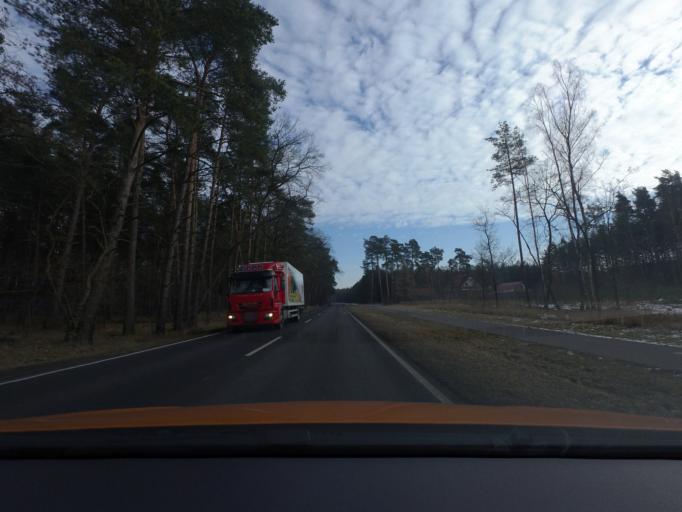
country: DE
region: Brandenburg
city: Ruthnick
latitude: 52.8997
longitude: 13.0696
